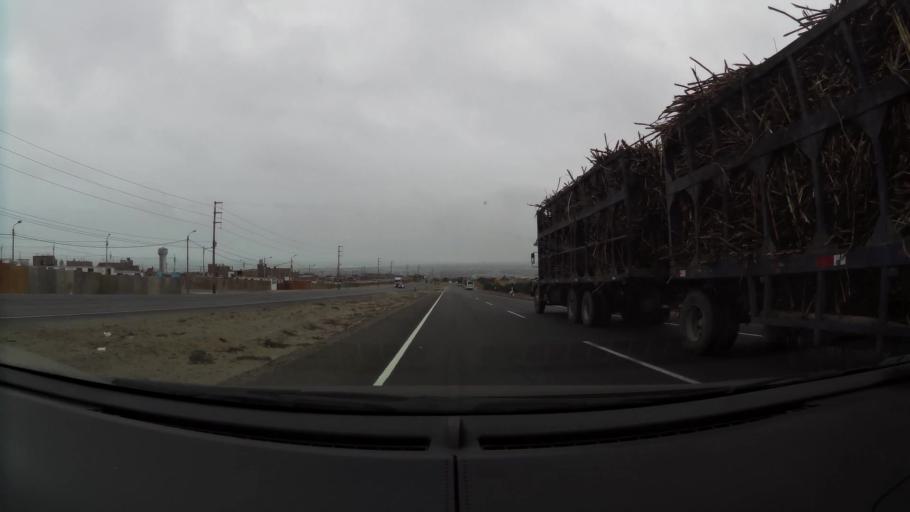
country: PE
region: La Libertad
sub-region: Provincia de Trujillo
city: Salaverry
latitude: -8.1880
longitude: -78.9793
